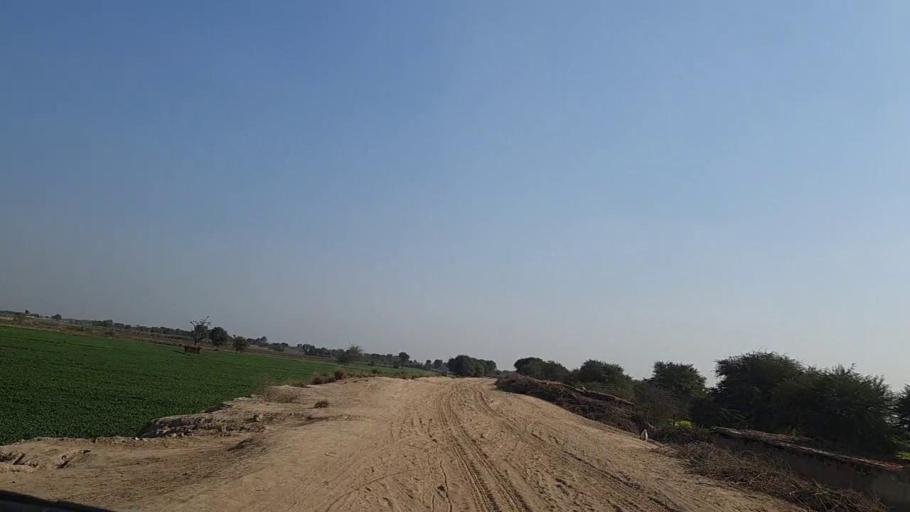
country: PK
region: Sindh
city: Sakrand
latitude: 26.0197
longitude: 68.3107
